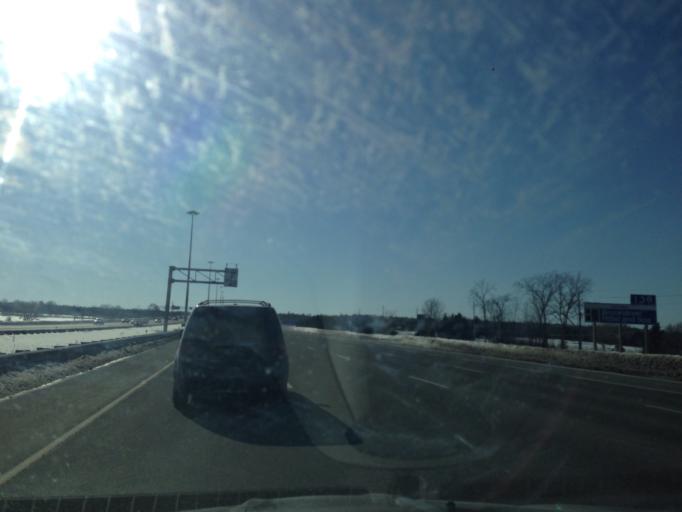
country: CA
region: Ontario
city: Bells Corners
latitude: 45.3363
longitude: -75.8469
